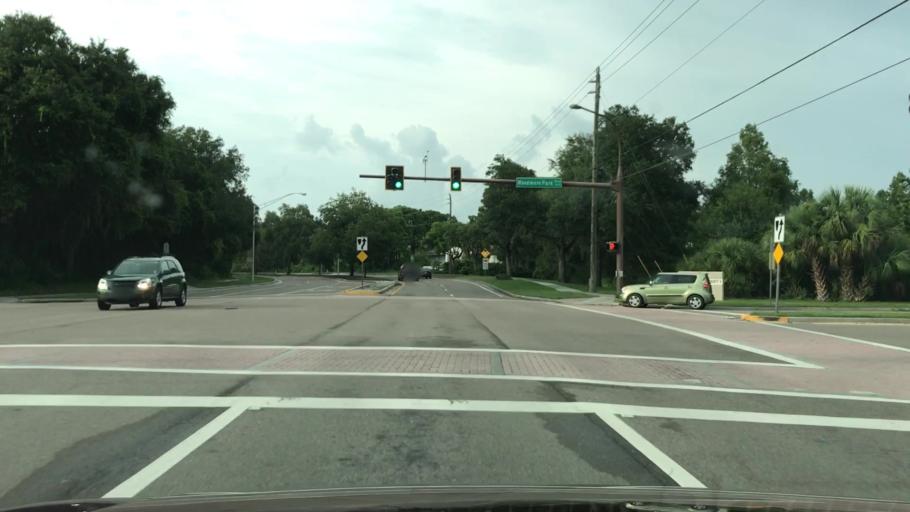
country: US
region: Florida
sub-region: Sarasota County
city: Venice Gardens
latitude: 27.0550
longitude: -82.3950
